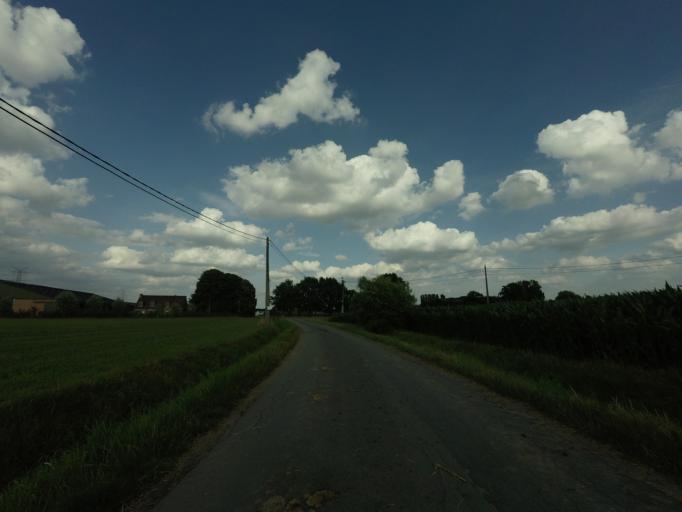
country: BE
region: Flanders
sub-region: Provincie Antwerpen
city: Kontich
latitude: 51.1123
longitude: 4.4665
